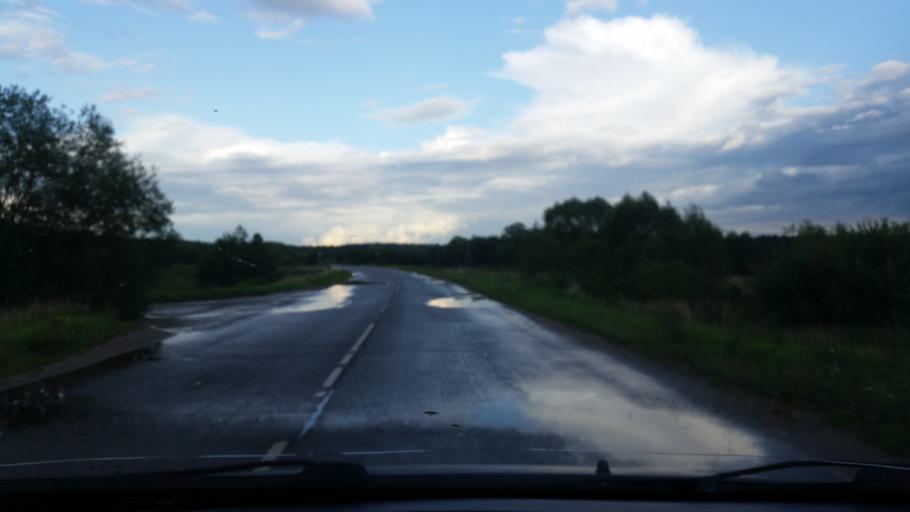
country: RU
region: Moskovskaya
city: Bol'shoye Gryzlovo
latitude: 54.8686
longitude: 37.8433
